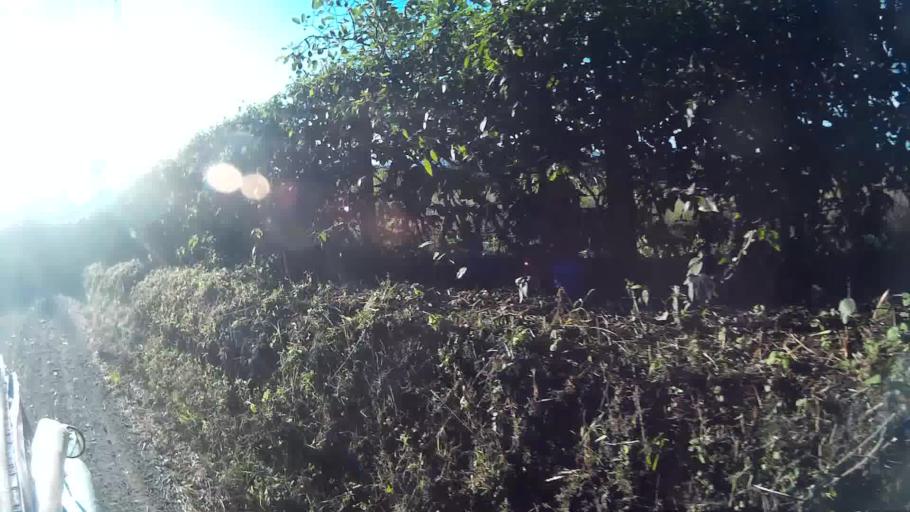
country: CO
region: Valle del Cauca
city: Ulloa
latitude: 4.7337
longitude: -75.6834
